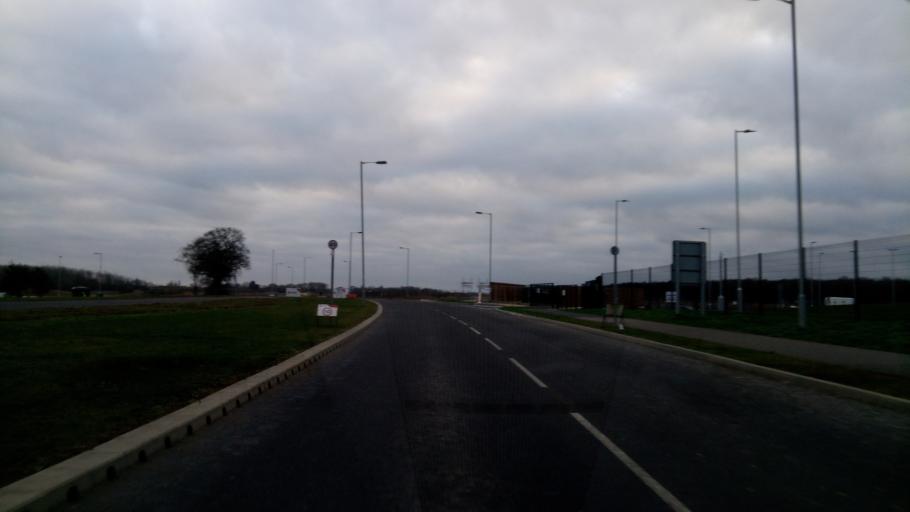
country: GB
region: England
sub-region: Cambridgeshire
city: Yaxley
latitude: 52.5329
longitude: -0.3032
